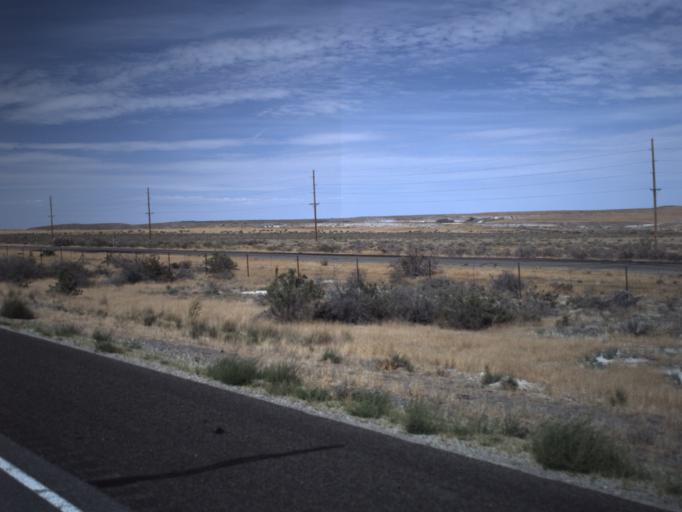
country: US
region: Utah
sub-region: Tooele County
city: Grantsville
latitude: 40.7293
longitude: -113.1253
